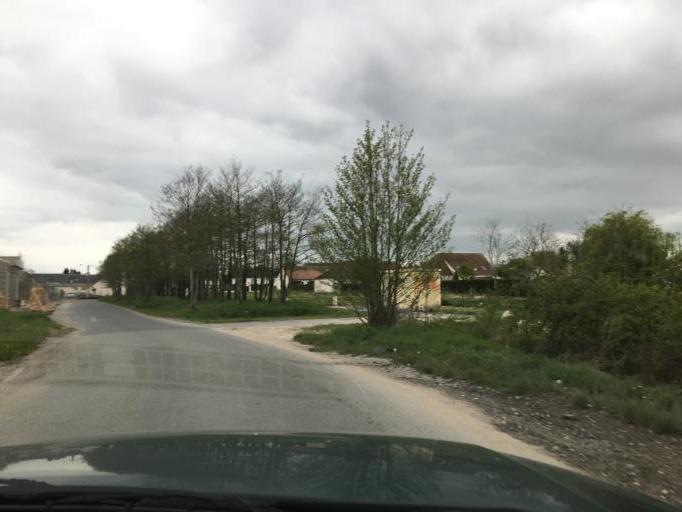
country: FR
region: Centre
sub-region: Departement du Loiret
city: Saint-Jean-de-la-Ruelle
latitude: 47.9233
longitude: 1.8717
